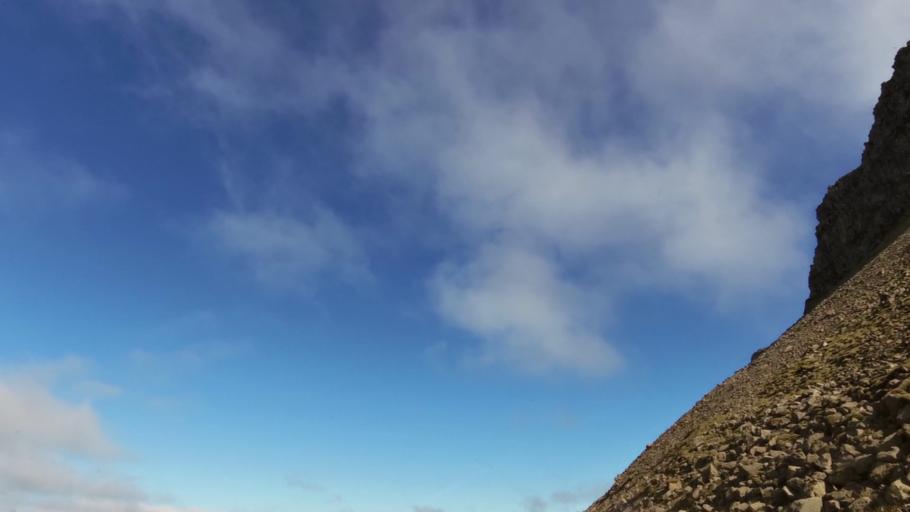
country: IS
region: West
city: Olafsvik
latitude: 65.5675
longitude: -24.0485
